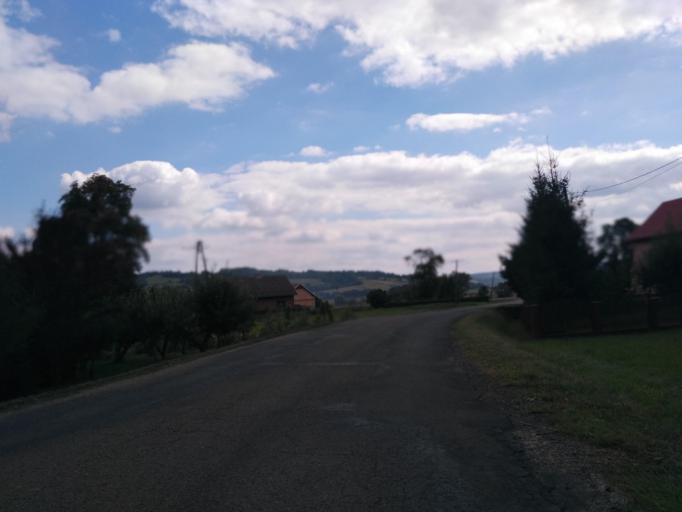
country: PL
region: Subcarpathian Voivodeship
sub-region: Powiat brzozowski
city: Nozdrzec
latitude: 49.7846
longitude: 22.2119
